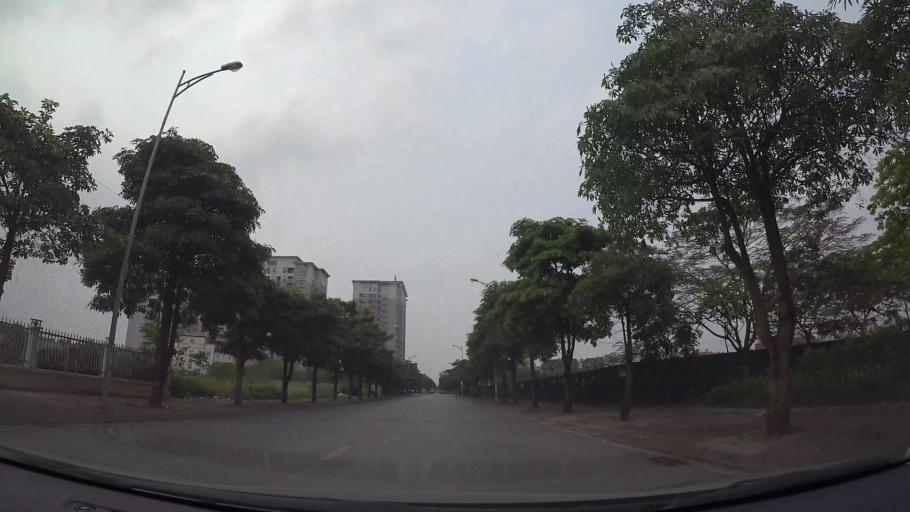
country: VN
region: Ha Noi
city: Trau Quy
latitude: 21.0568
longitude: 105.9083
